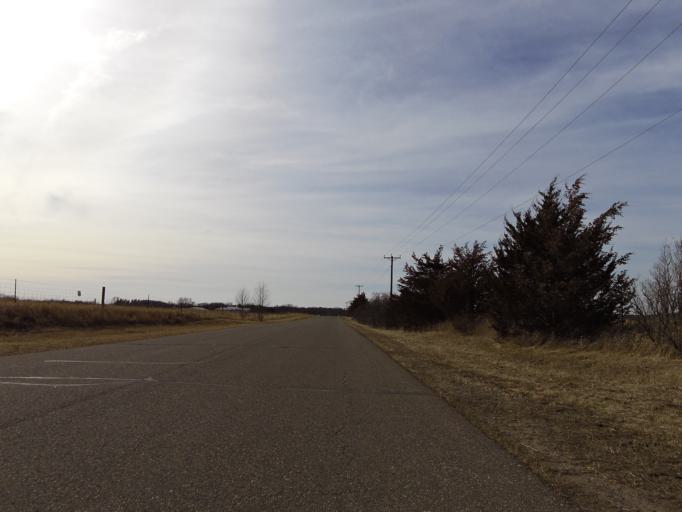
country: US
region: Minnesota
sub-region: Washington County
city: Lakeland
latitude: 44.9489
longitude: -92.7873
